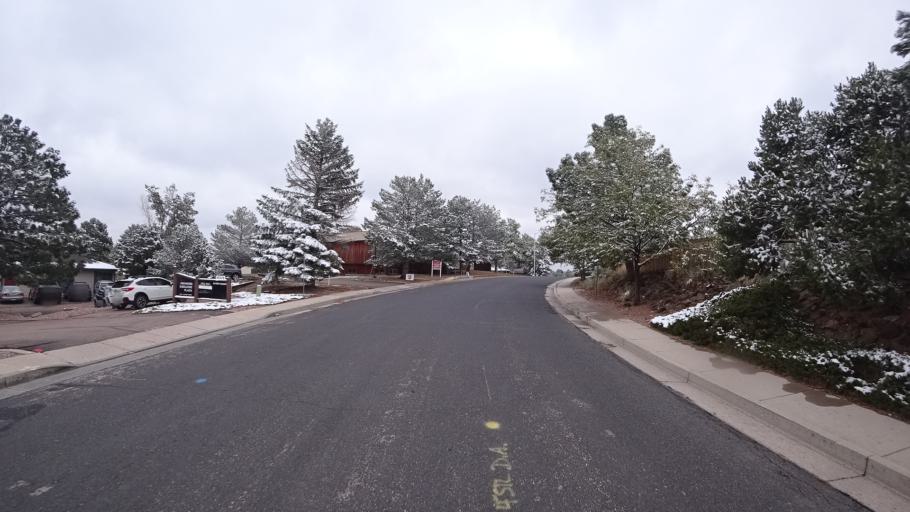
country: US
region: Colorado
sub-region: El Paso County
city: Colorado Springs
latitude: 38.9188
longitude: -104.7895
